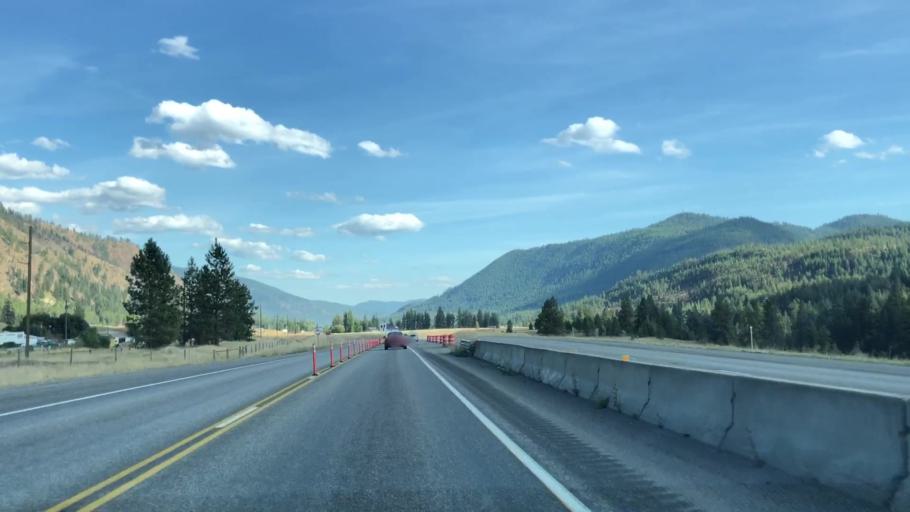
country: US
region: Montana
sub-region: Mineral County
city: Superior
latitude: 47.2140
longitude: -114.9429
